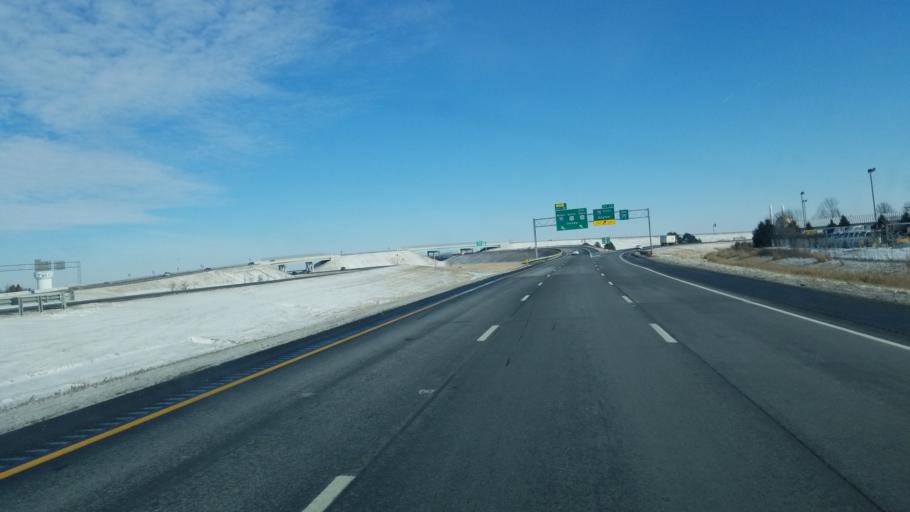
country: US
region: Ohio
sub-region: Wood County
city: Perrysburg
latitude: 41.5321
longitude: -83.6283
